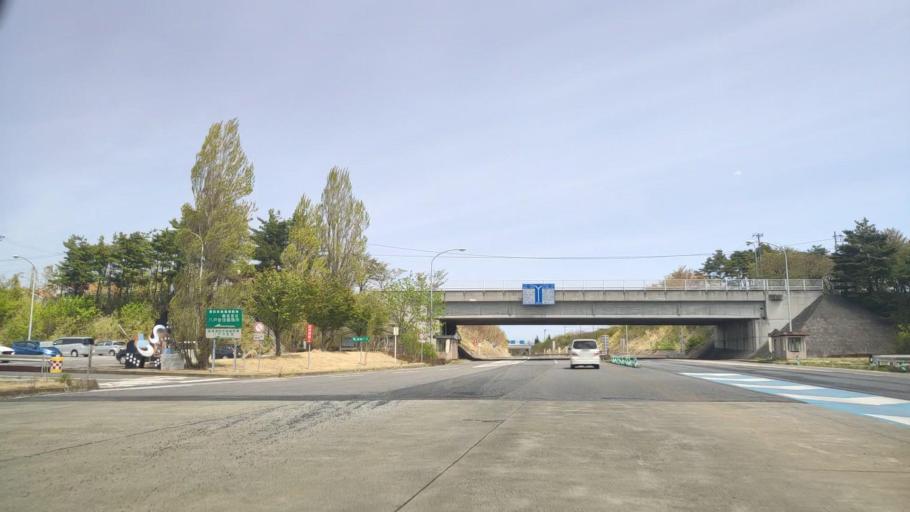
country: JP
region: Aomori
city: Hachinohe
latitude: 40.4866
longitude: 141.4628
